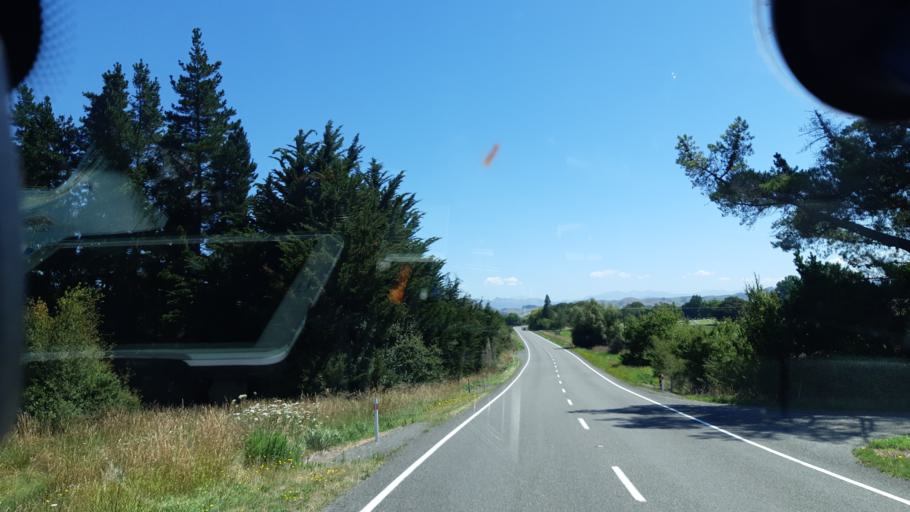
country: NZ
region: Canterbury
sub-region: Kaikoura District
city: Kaikoura
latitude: -42.7458
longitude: 173.2671
